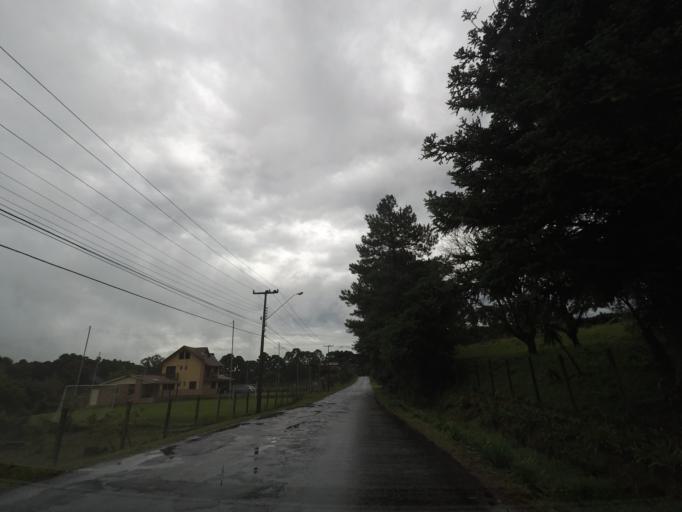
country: BR
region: Parana
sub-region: Campo Largo
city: Campo Largo
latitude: -25.4510
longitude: -49.4443
